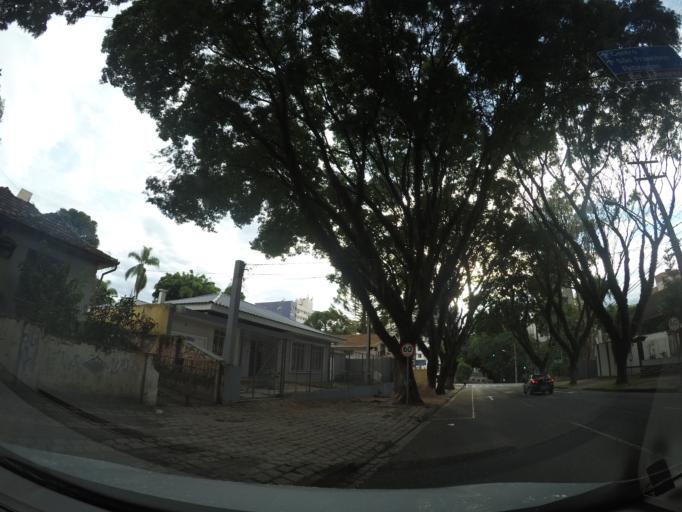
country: BR
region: Parana
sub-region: Curitiba
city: Curitiba
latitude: -25.4239
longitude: -49.2892
